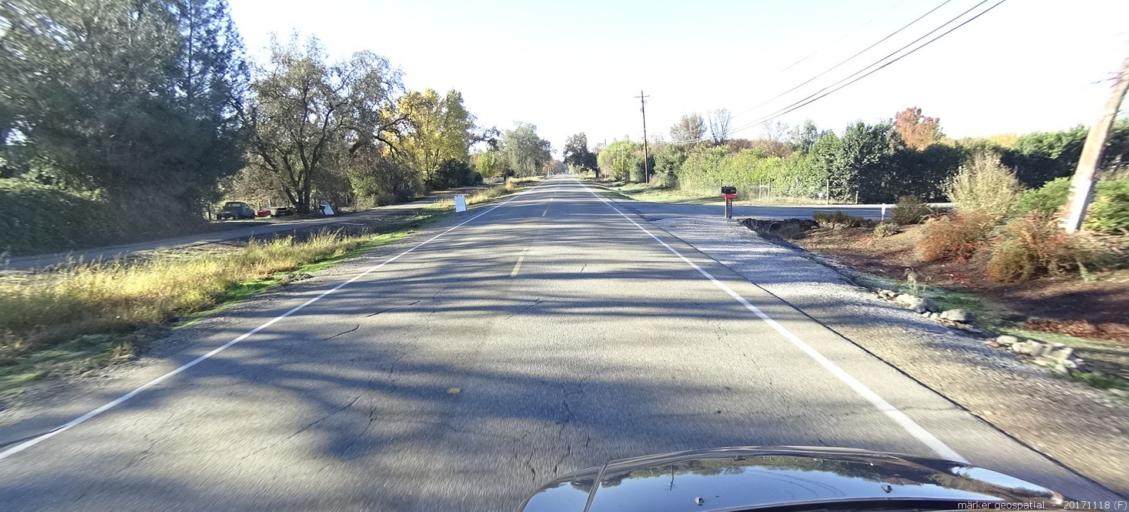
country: US
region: California
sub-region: Shasta County
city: Anderson
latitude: 40.4515
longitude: -122.2531
